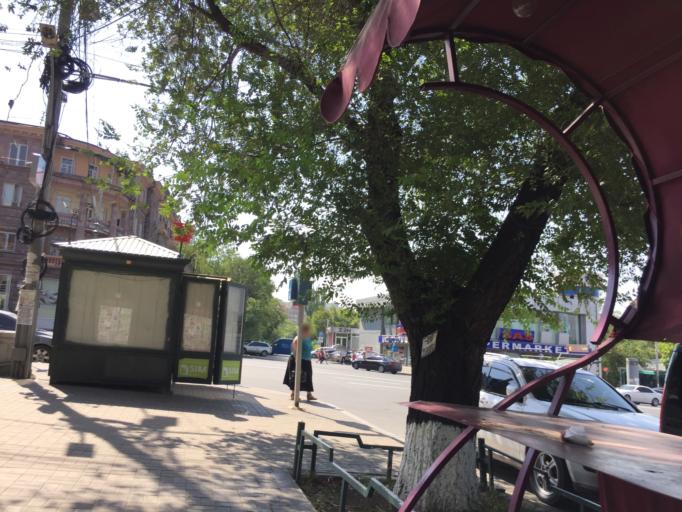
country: AM
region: Yerevan
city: Yerevan
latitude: 40.1871
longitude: 44.5223
